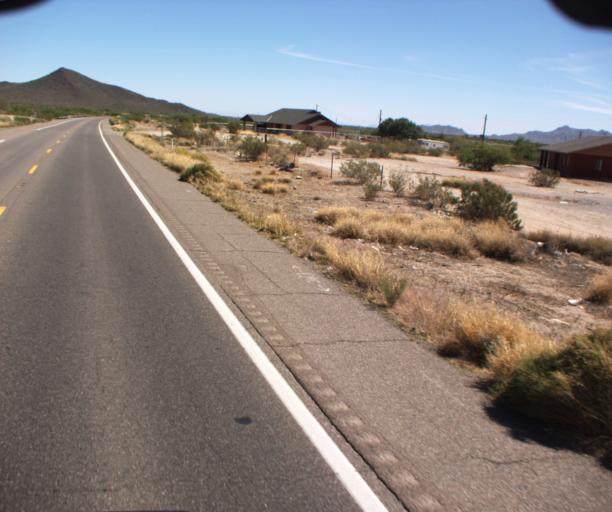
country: US
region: Arizona
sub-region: Pinal County
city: Sacaton
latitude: 33.1203
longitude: -111.7345
